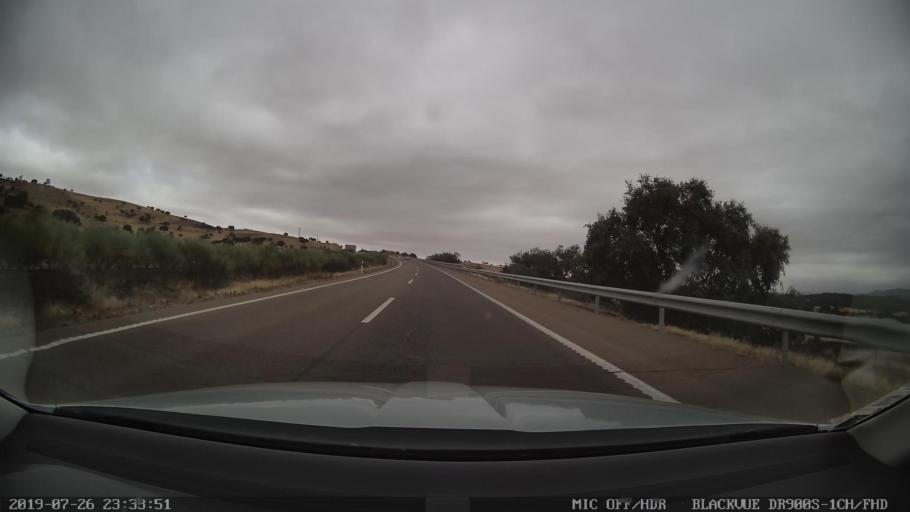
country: ES
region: Extremadura
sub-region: Provincia de Caceres
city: Santa Cruz de la Sierra
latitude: 39.3490
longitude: -5.8582
